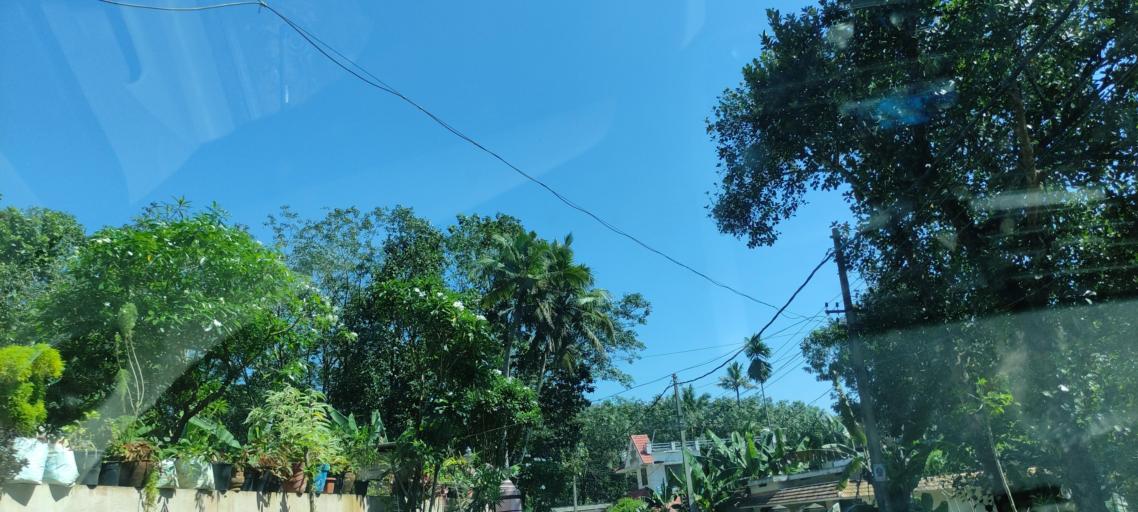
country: IN
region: Kerala
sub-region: Pattanamtitta
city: Adur
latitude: 9.0948
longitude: 76.7358
